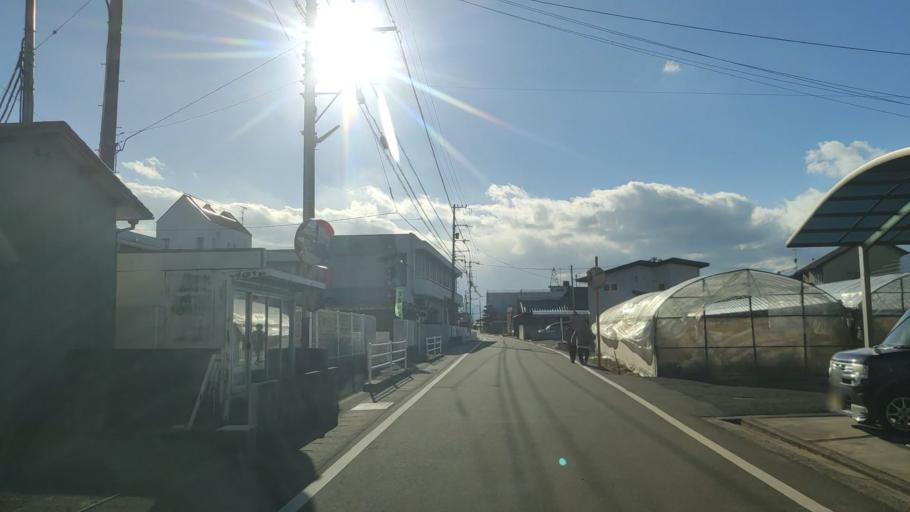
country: JP
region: Ehime
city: Saijo
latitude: 33.9139
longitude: 133.1011
